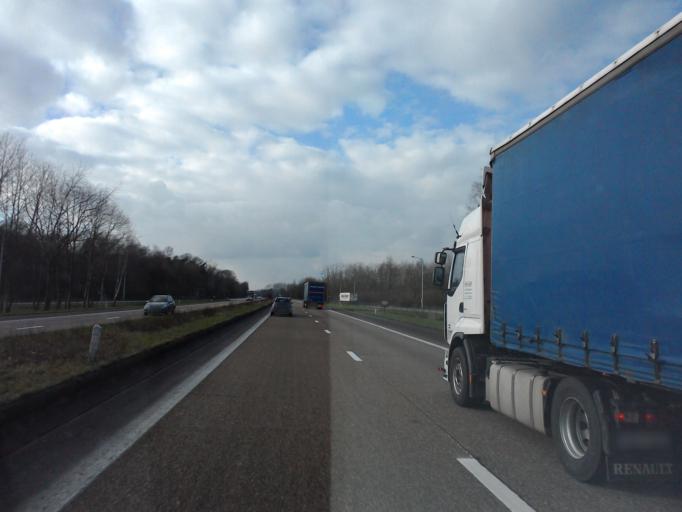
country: BE
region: Flanders
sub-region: Provincie Antwerpen
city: Oud-Turnhout
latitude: 51.2983
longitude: 4.9759
